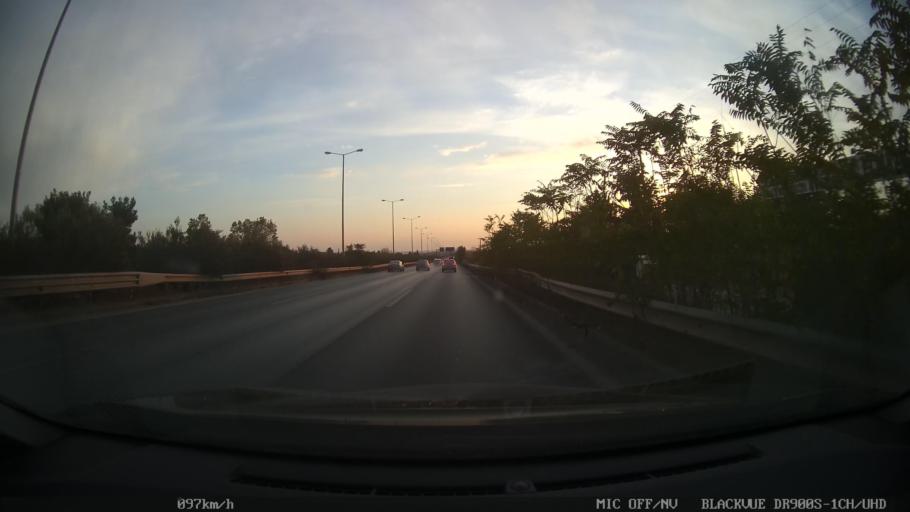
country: GR
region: Central Macedonia
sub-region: Nomos Thessalonikis
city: Pylaia
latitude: 40.5892
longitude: 22.9874
